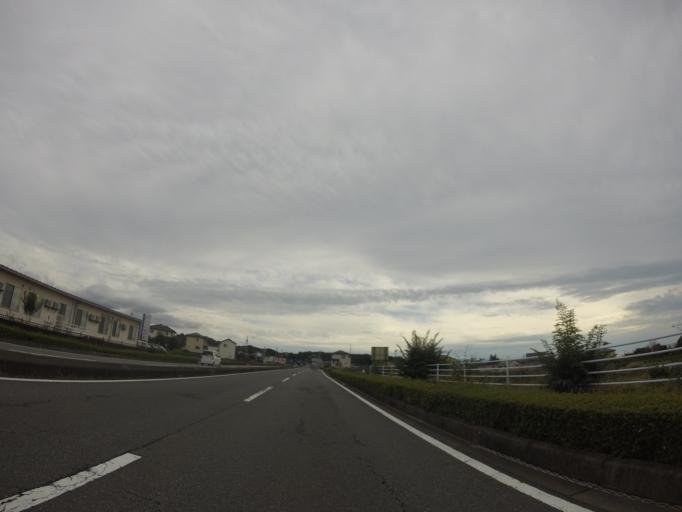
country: JP
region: Shizuoka
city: Fuji
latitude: 35.1993
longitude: 138.6785
